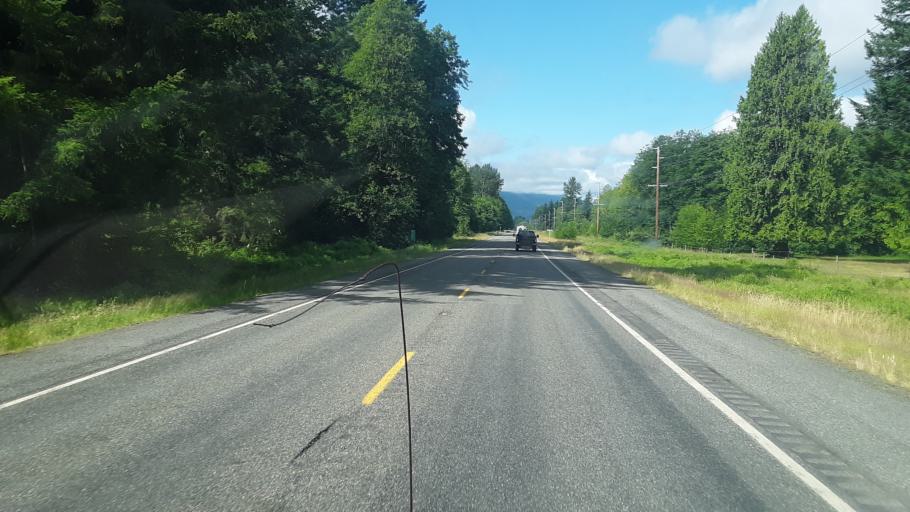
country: US
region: Washington
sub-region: Lewis County
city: Morton
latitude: 46.5614
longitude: -121.7187
